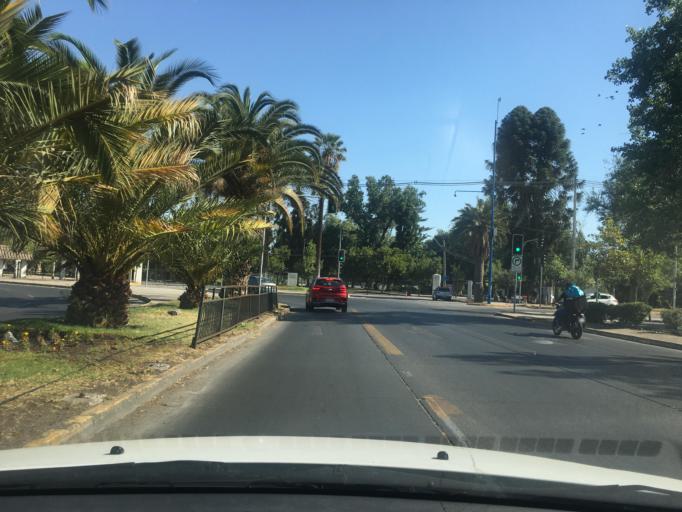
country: CL
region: Santiago Metropolitan
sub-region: Provincia de Santiago
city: Santiago
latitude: -33.4580
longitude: -70.6604
